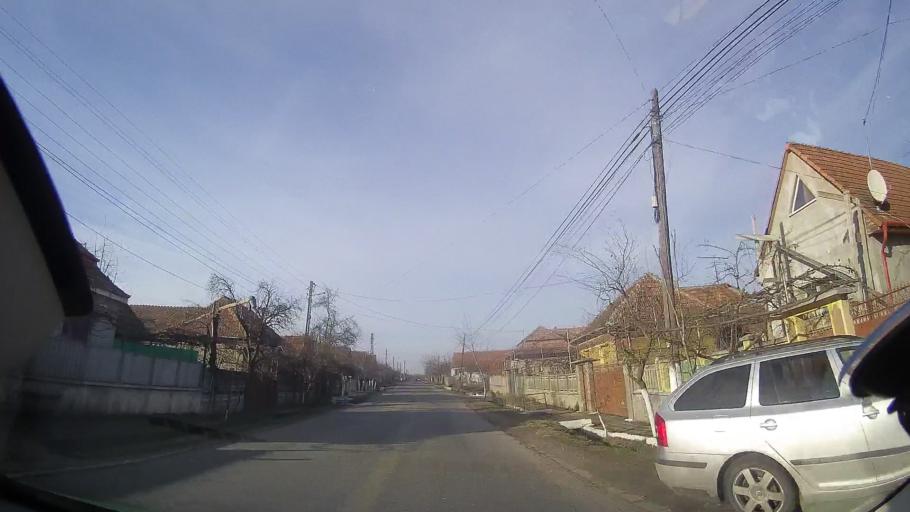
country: RO
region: Bihor
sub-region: Comuna Brusturi
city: Brusturi
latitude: 47.1518
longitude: 22.2482
